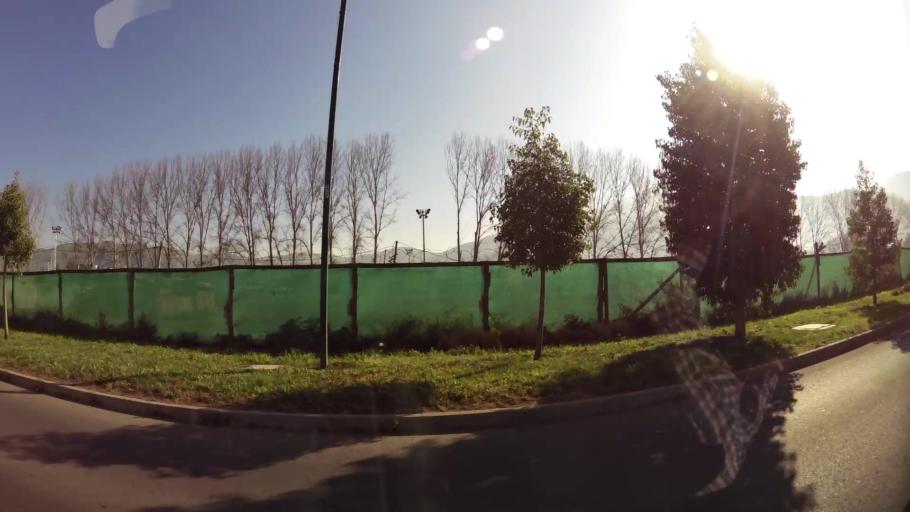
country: CL
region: Santiago Metropolitan
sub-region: Provincia de Chacabuco
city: Chicureo Abajo
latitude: -33.3620
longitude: -70.6676
